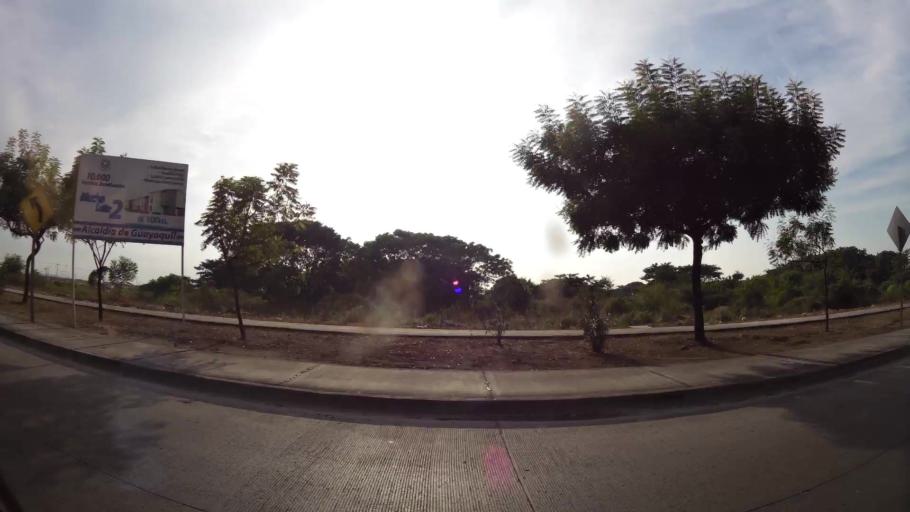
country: EC
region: Guayas
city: Eloy Alfaro
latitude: -2.0719
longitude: -79.8975
